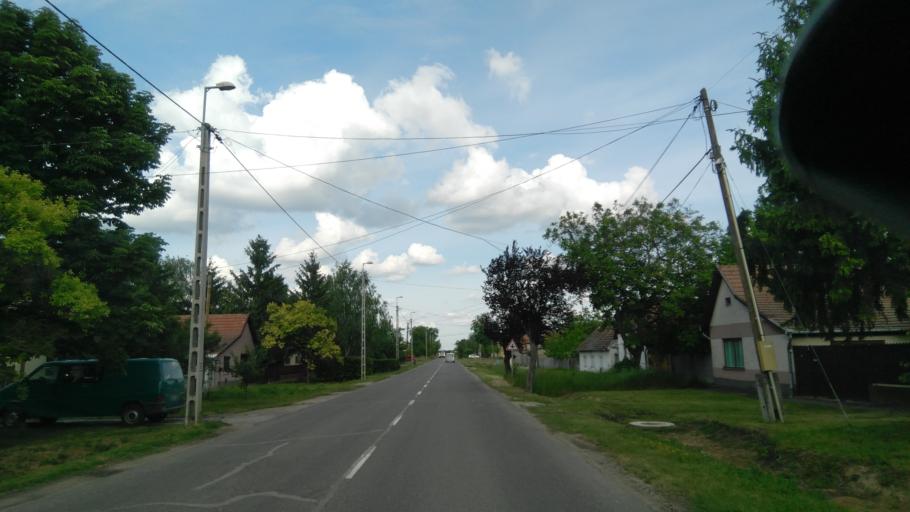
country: HU
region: Bekes
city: Battonya
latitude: 46.2926
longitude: 21.0281
